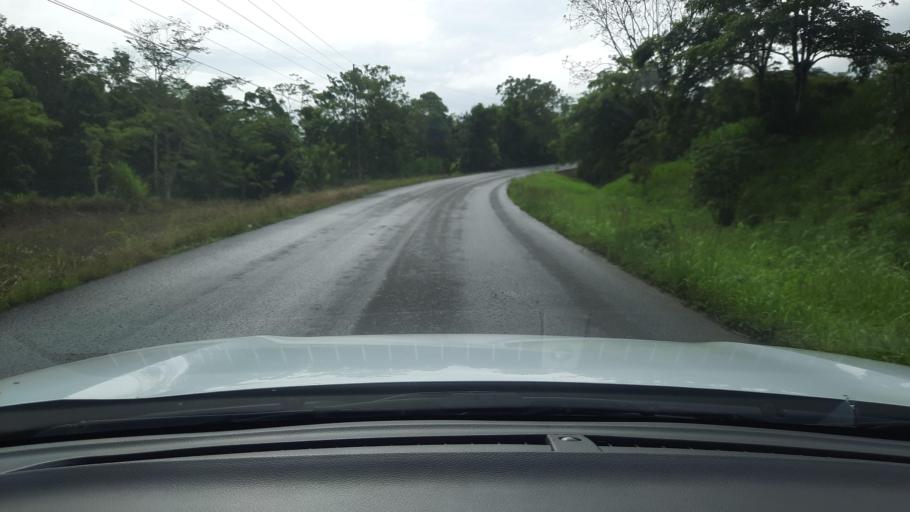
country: CR
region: Alajuela
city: San Jose
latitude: 10.9442
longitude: -85.1181
